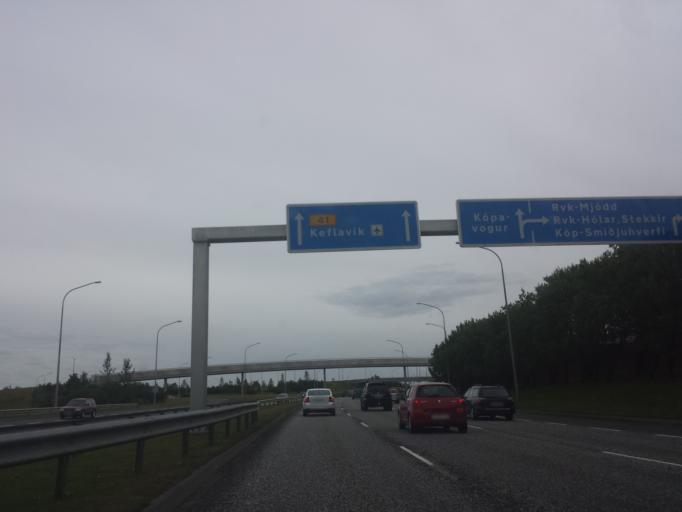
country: IS
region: Capital Region
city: Reykjavik
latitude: 64.1166
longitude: -21.8441
